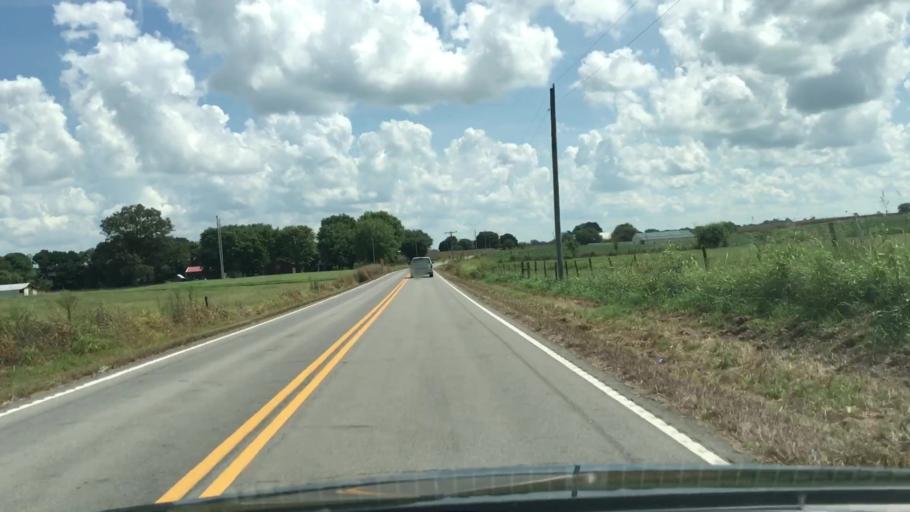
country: US
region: Tennessee
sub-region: Robertson County
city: Springfield
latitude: 36.5850
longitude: -86.8870
